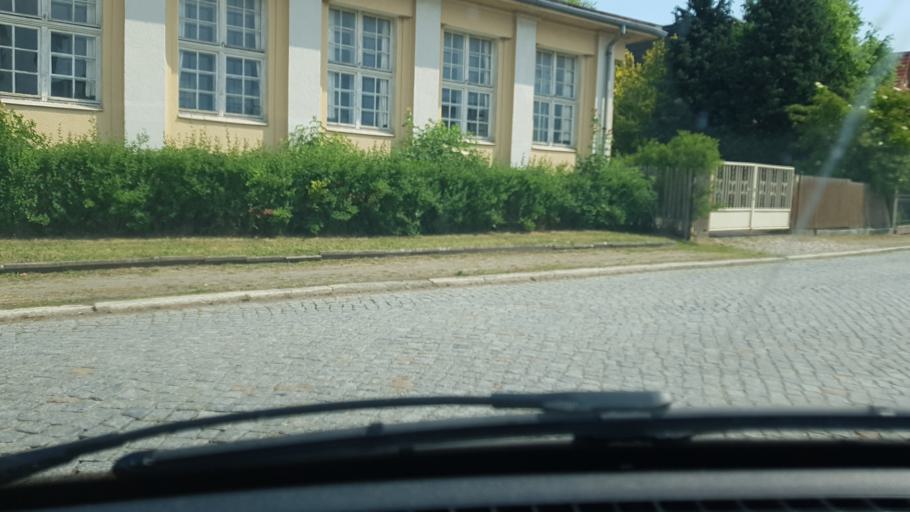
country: DE
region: Saxony-Anhalt
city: Osterwieck
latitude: 51.9695
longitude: 10.7174
